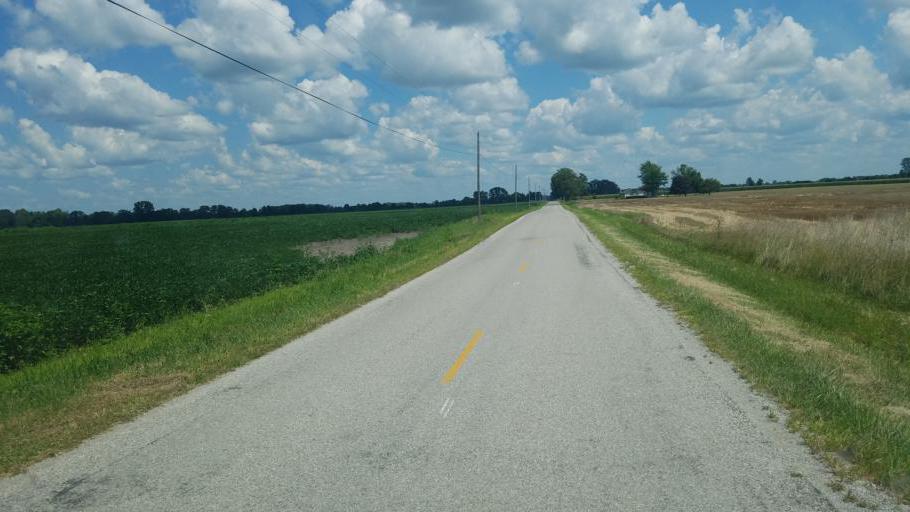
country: US
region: Ohio
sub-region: Marion County
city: Marion
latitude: 40.6377
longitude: -83.0111
